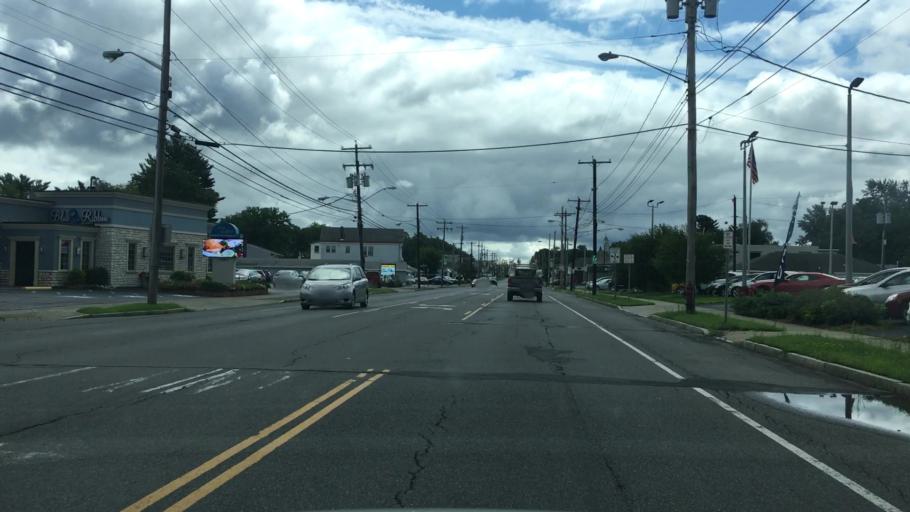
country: US
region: New York
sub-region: Schenectady County
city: Schenectady
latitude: 42.7808
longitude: -73.9045
